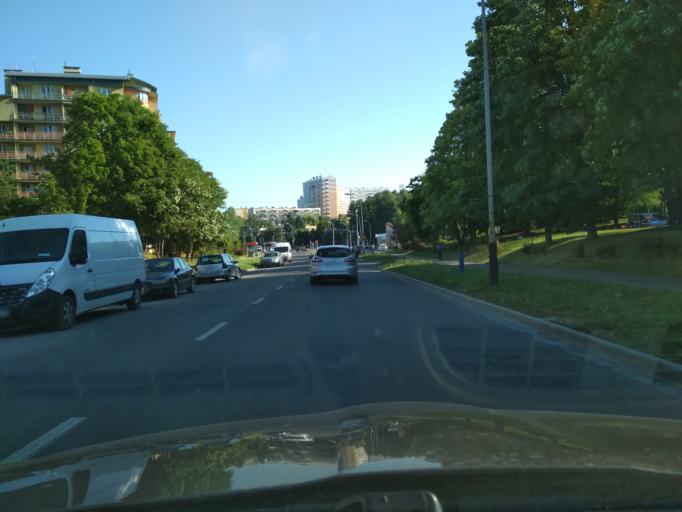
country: PL
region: Subcarpathian Voivodeship
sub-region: Rzeszow
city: Rzeszow
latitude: 50.0541
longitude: 21.9785
